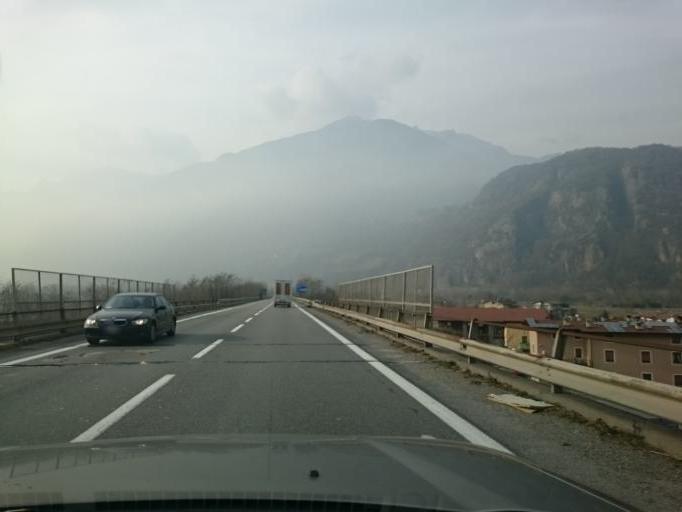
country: IT
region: Lombardy
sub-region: Provincia di Brescia
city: Gianico
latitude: 45.8721
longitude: 10.1717
